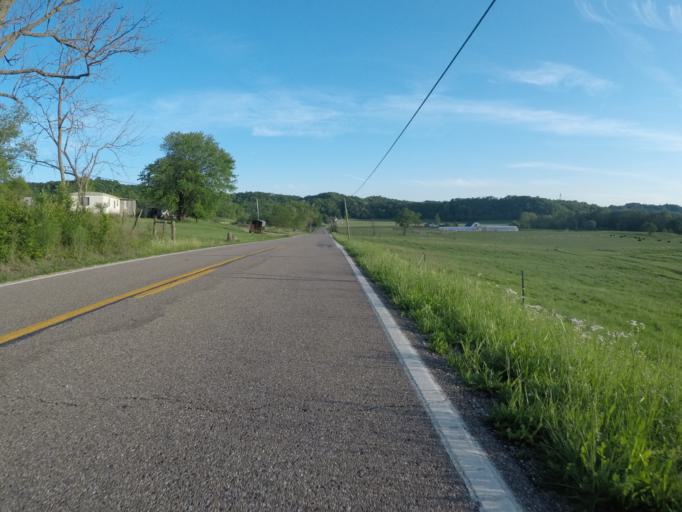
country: US
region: West Virginia
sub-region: Cabell County
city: Huntington
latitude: 38.5312
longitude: -82.4596
